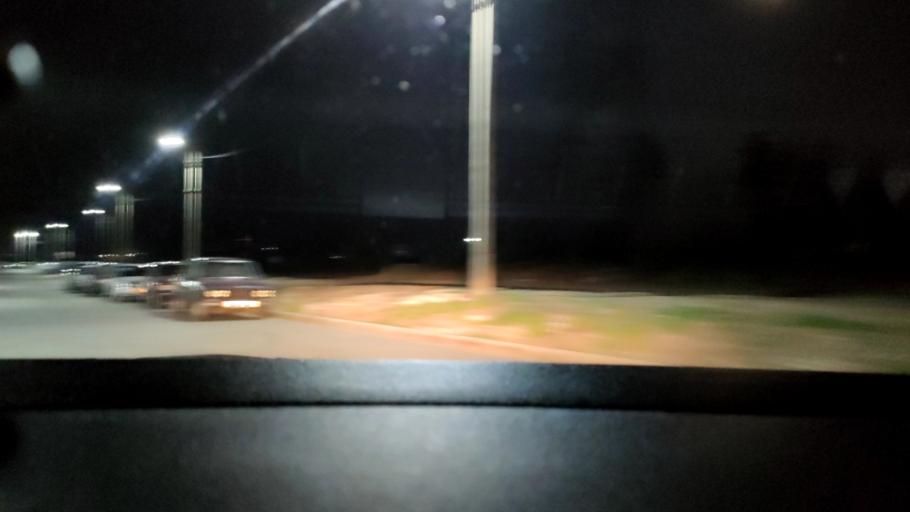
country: RU
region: Voronezj
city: Maslovka
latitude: 51.5887
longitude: 39.2422
